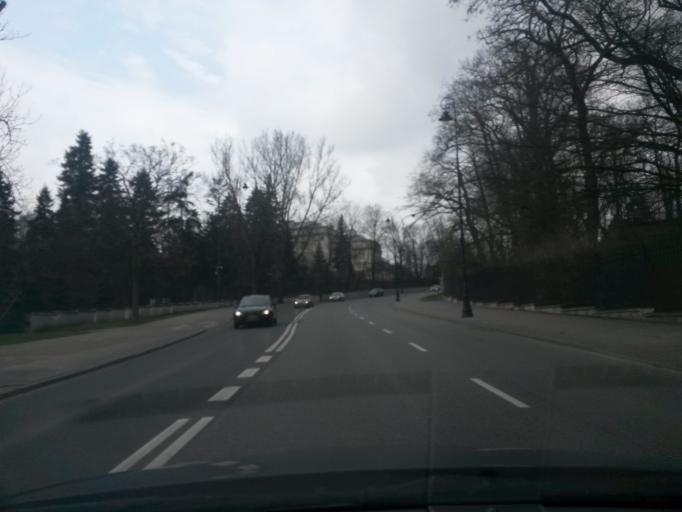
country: PL
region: Masovian Voivodeship
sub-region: Warszawa
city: Mokotow
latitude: 52.2111
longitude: 21.0273
